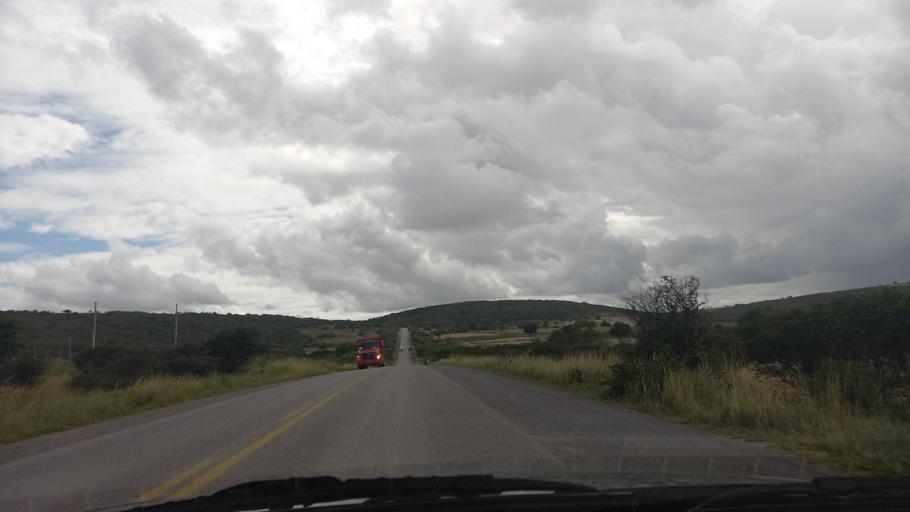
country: BR
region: Pernambuco
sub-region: Lajedo
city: Lajedo
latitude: -8.6714
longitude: -36.3880
